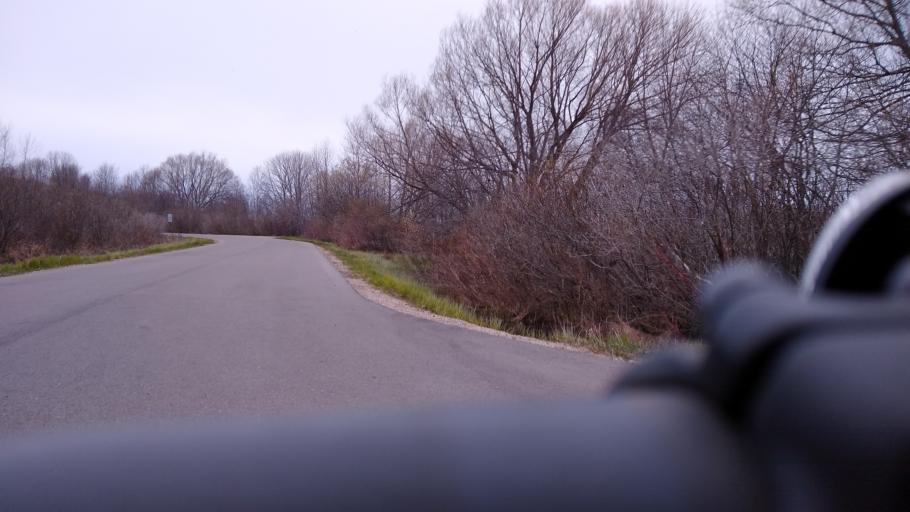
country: US
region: Michigan
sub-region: Delta County
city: Escanaba
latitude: 45.7065
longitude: -87.0799
